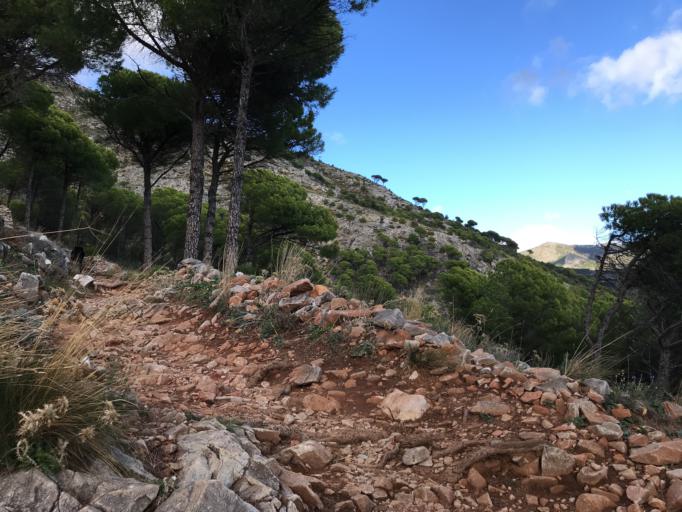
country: ES
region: Andalusia
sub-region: Provincia de Malaga
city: Mijas
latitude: 36.5975
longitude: -4.6396
